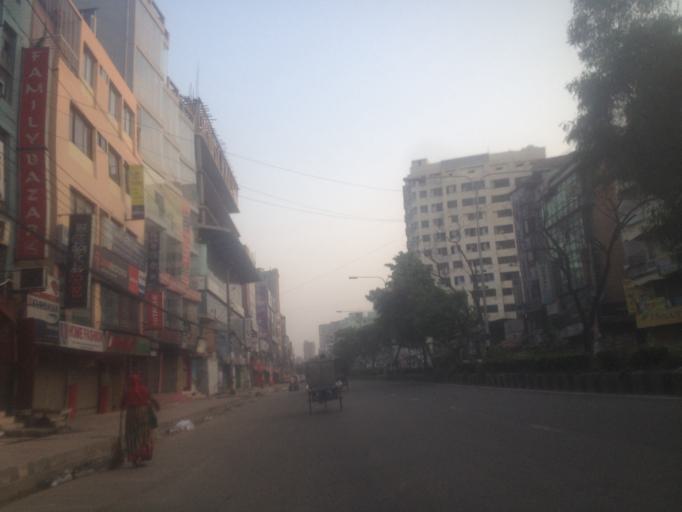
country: BD
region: Dhaka
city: Azimpur
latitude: 23.8014
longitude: 90.3710
